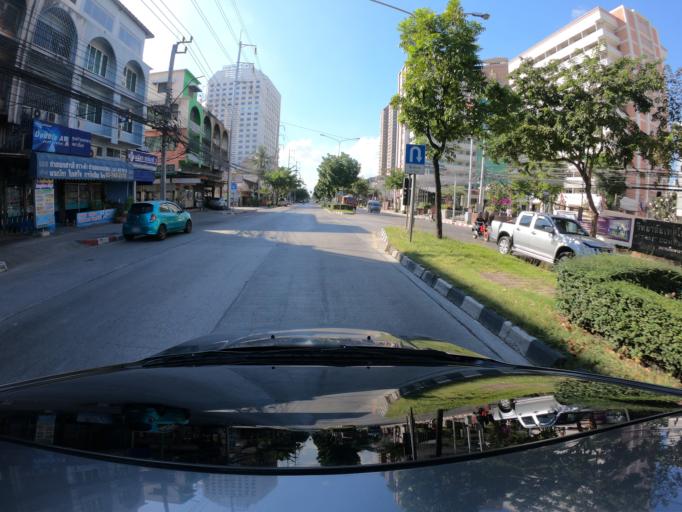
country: TH
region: Bangkok
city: Phra Khanong
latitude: 13.6741
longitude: 100.6015
